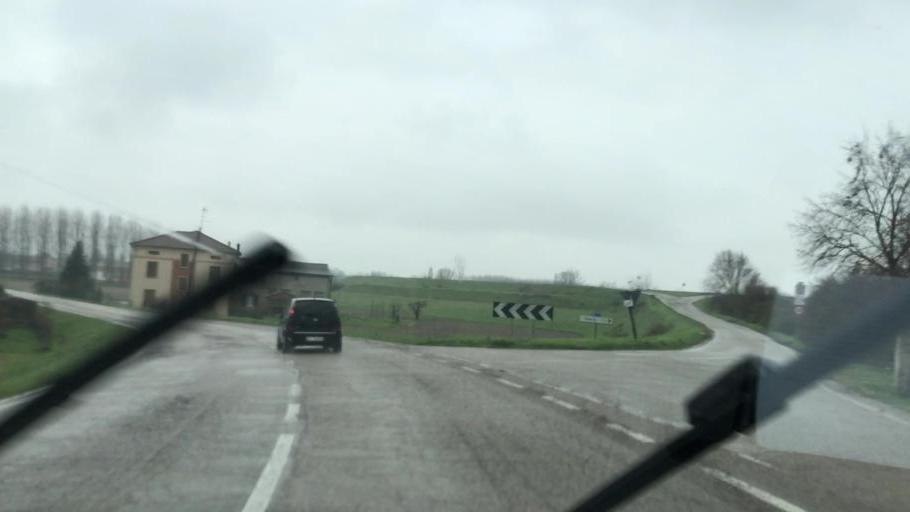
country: IT
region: Lombardy
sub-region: Provincia di Mantova
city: Borgofranco sul Po
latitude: 45.0449
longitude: 11.2135
